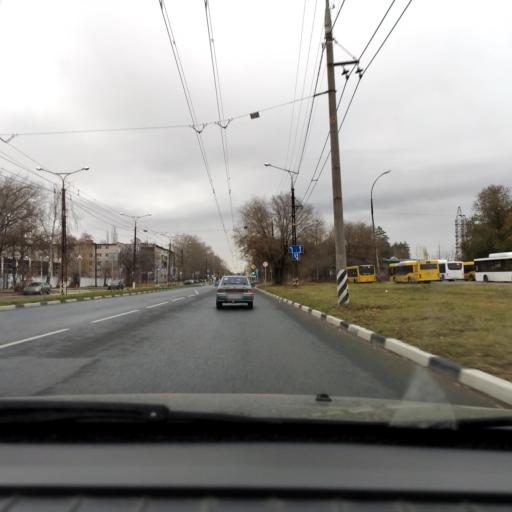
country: RU
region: Samara
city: Tol'yatti
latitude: 53.4984
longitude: 49.3995
